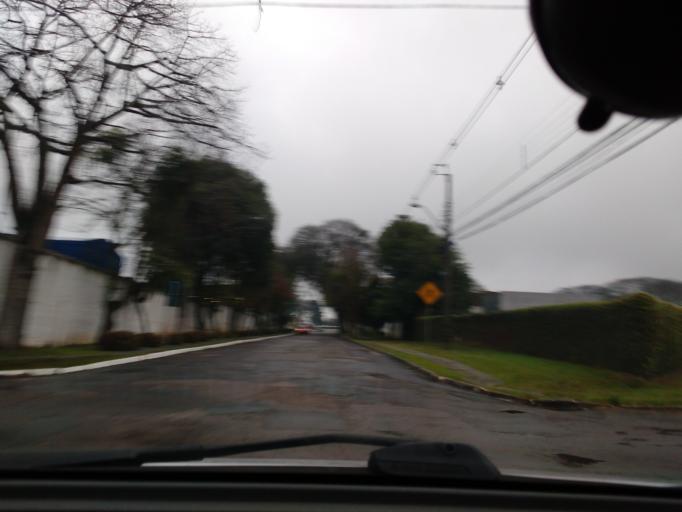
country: BR
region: Parana
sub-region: Pinhais
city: Pinhais
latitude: -25.4264
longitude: -49.2291
